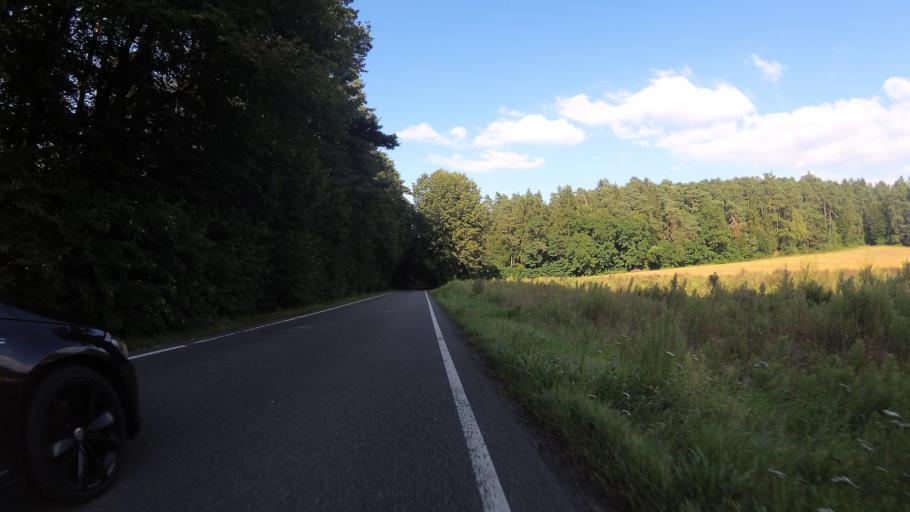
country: DE
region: Saarland
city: Bexbach
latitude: 49.3254
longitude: 7.2466
